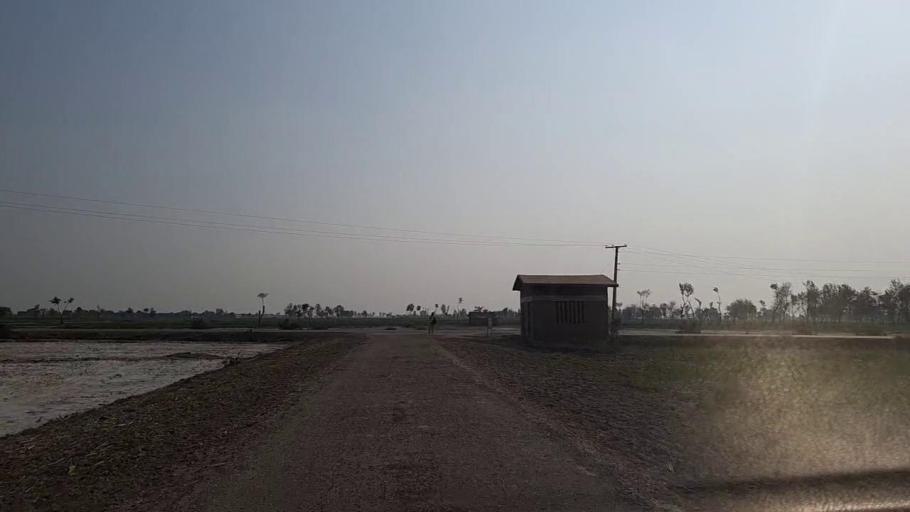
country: PK
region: Sindh
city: Daur
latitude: 26.4096
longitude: 68.4125
